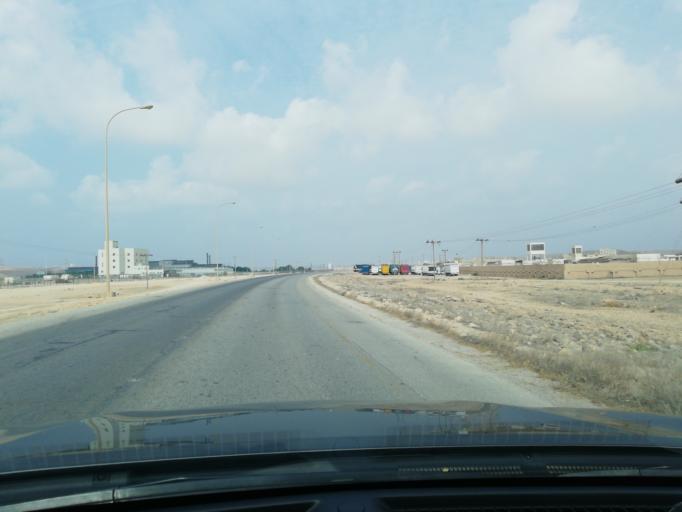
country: OM
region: Zufar
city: Salalah
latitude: 16.9497
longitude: 53.9800
